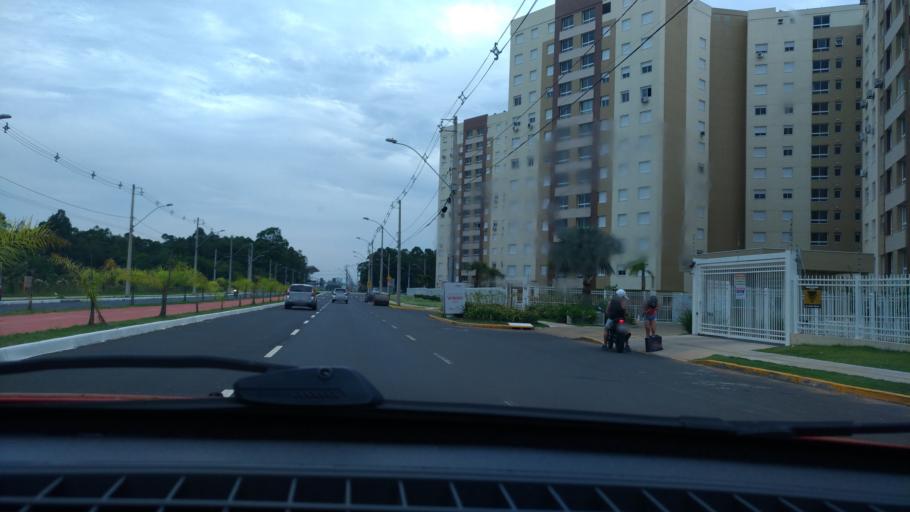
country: BR
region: Rio Grande do Sul
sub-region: Canoas
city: Canoas
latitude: -29.9082
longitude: -51.1652
